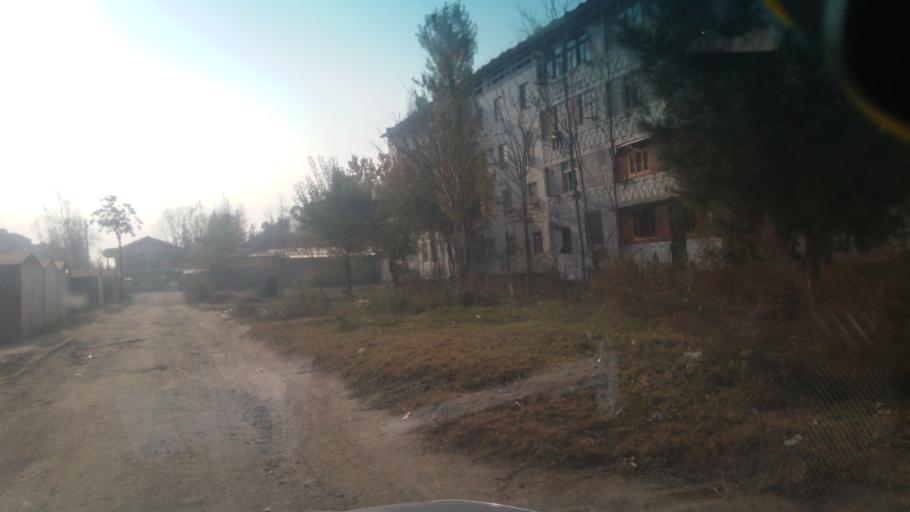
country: UZ
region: Sirdaryo
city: Guliston
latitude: 40.5196
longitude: 68.7755
